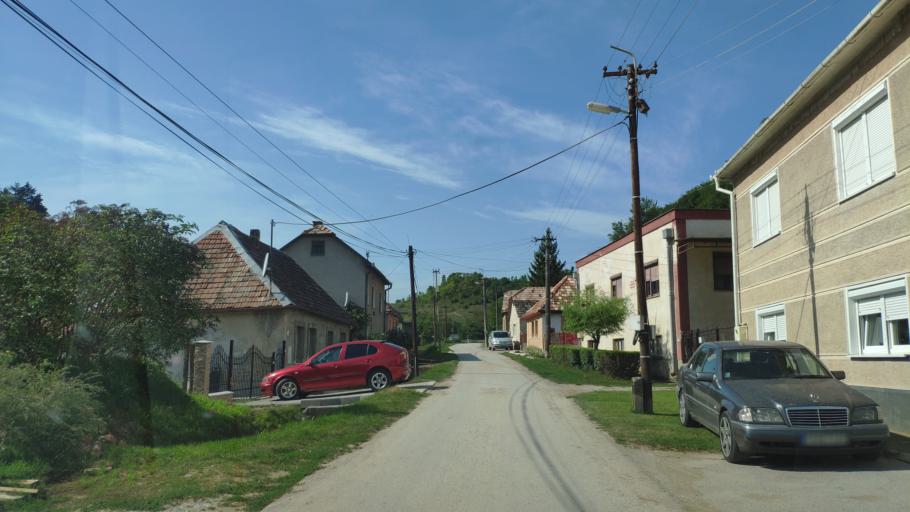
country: HU
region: Borsod-Abauj-Zemplen
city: Putnok
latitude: 48.4531
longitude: 20.3151
